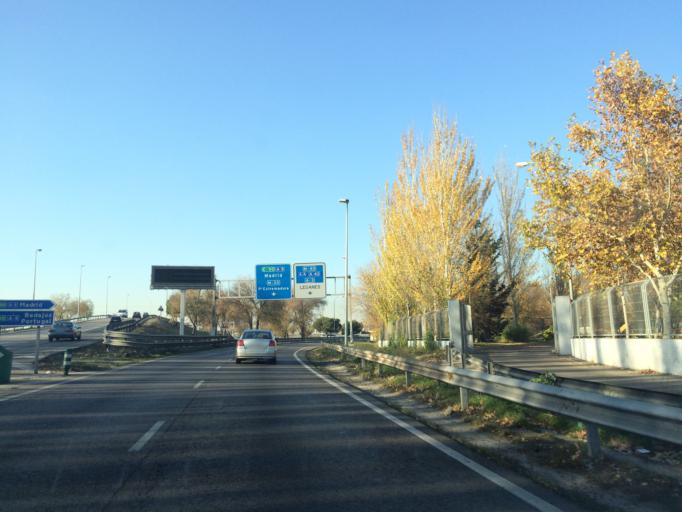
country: ES
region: Madrid
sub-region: Provincia de Madrid
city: Alcorcon
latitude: 40.3590
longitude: -3.8131
